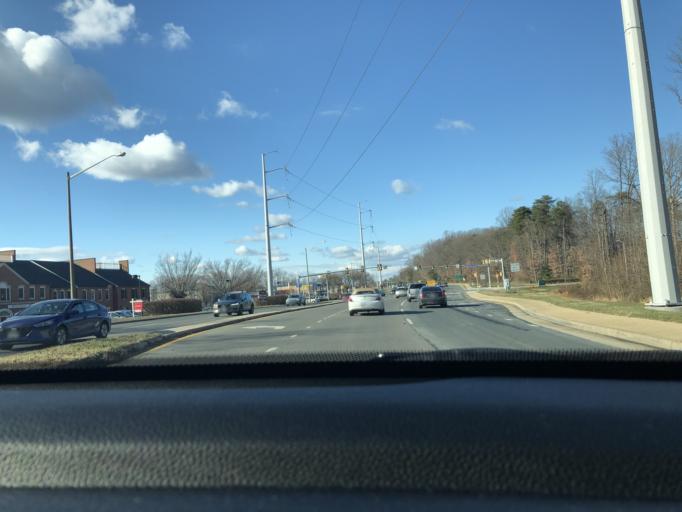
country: US
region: Virginia
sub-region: City of Fairfax
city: Fairfax
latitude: 38.8248
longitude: -77.3112
